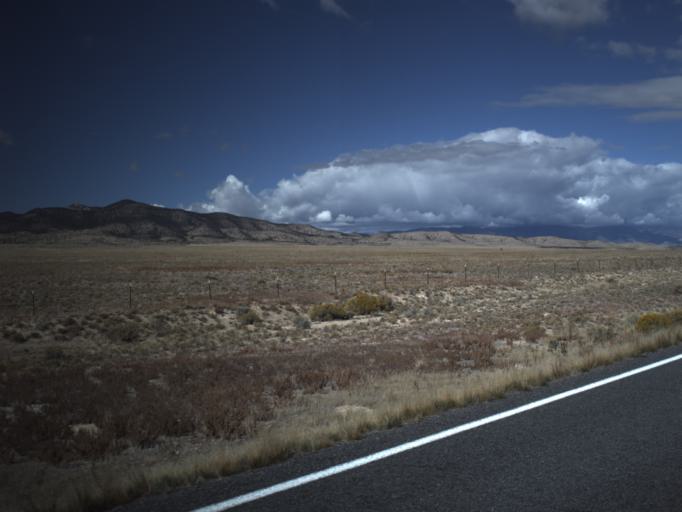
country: US
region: Utah
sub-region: Beaver County
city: Milford
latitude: 38.6406
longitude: -113.8614
